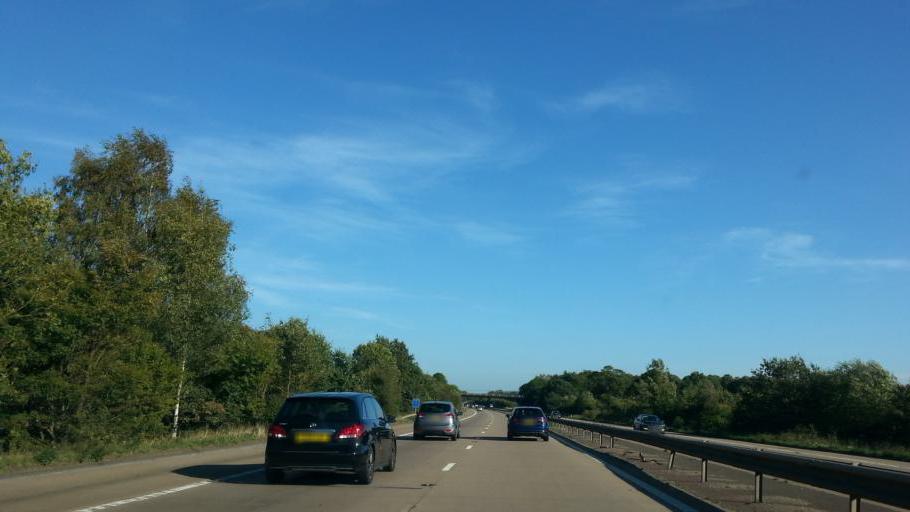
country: GB
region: England
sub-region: Staffordshire
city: Brewood
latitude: 52.6401
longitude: -2.1562
